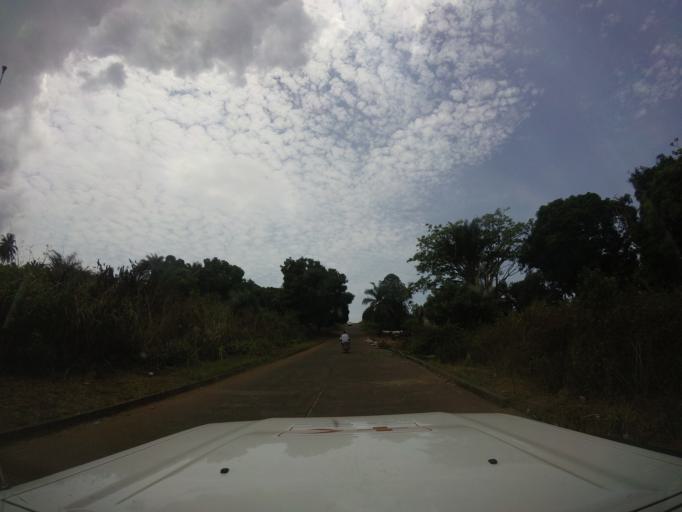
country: LR
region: Grand Cape Mount
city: Robertsport
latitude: 6.7522
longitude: -11.3747
